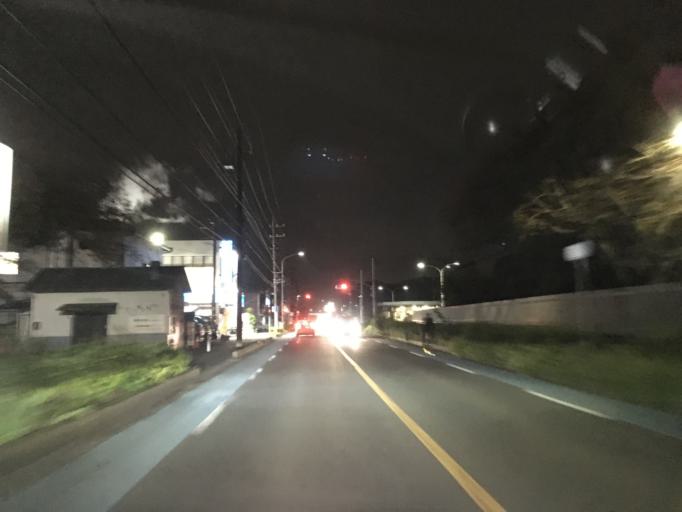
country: JP
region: Saitama
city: Sayama
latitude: 35.8456
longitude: 139.4211
